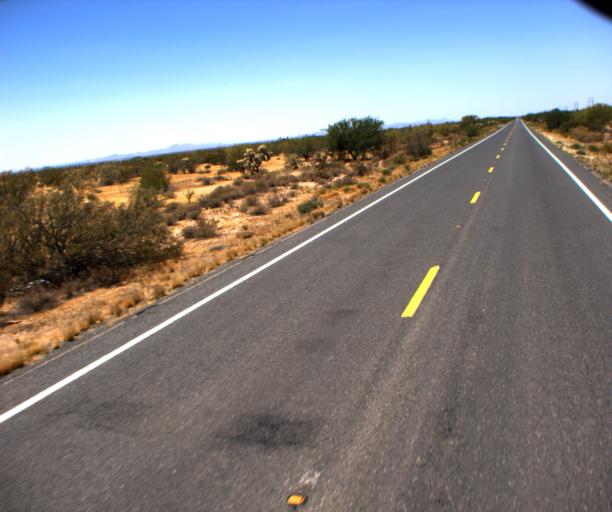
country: US
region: Arizona
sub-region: Pinal County
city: Florence
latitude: 32.8729
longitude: -111.2521
